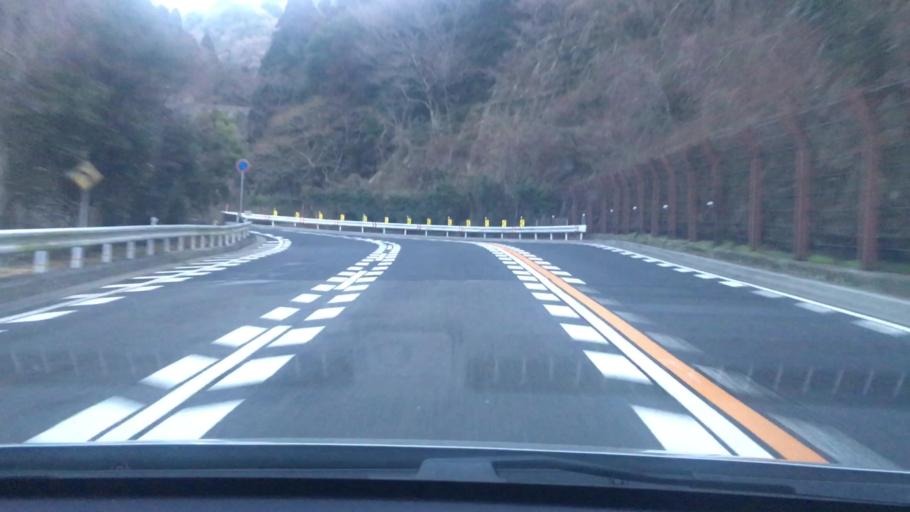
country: JP
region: Hyogo
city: Kobe
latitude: 34.7449
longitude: 135.2293
